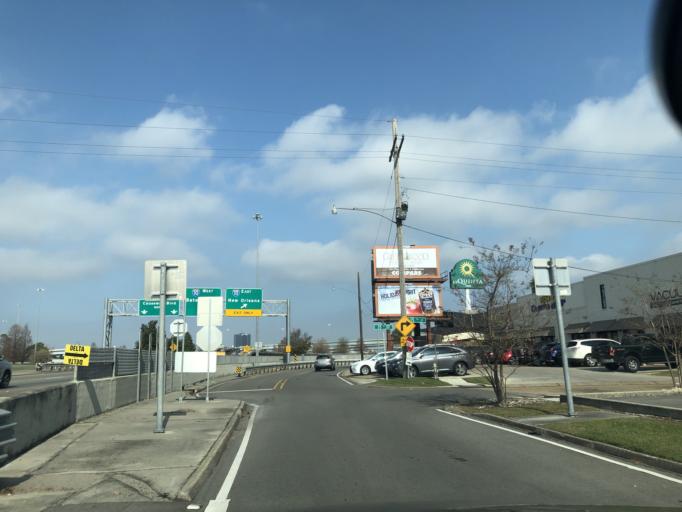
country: US
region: Louisiana
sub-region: Jefferson Parish
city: Metairie
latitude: 29.9938
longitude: -90.1554
